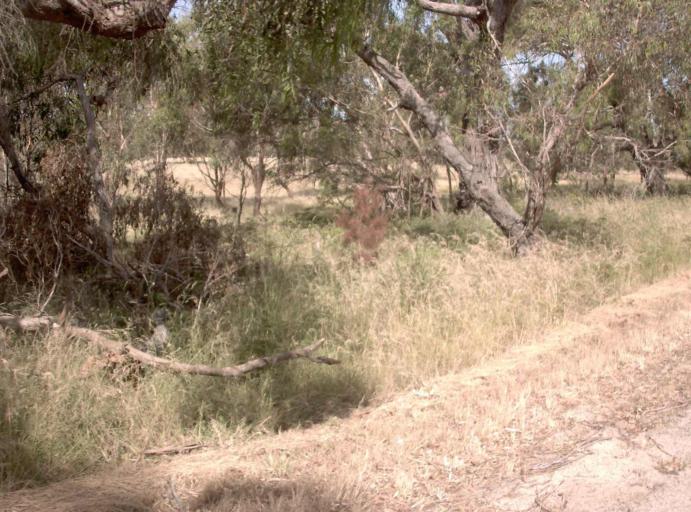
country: AU
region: Victoria
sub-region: Wellington
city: Sale
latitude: -38.2555
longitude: 147.1378
